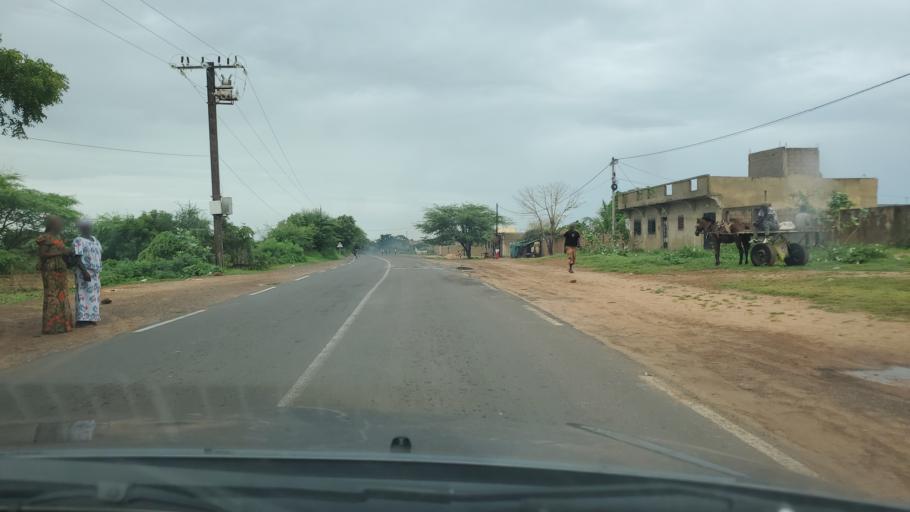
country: SN
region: Thies
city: Mekhe
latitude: 15.1284
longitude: -16.8625
